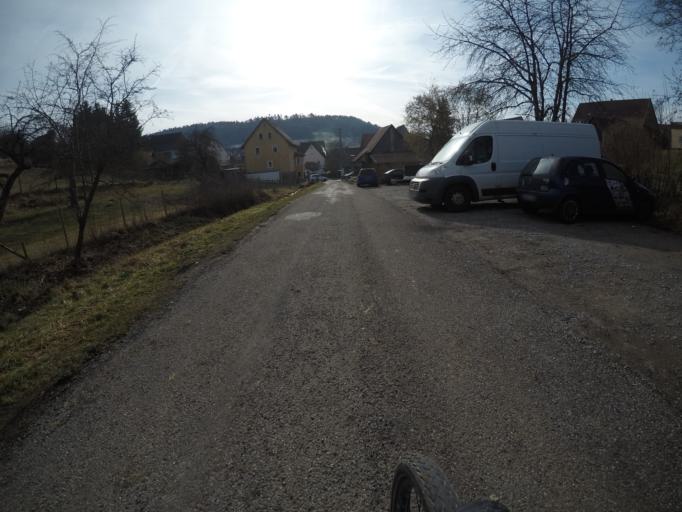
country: DE
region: Baden-Wuerttemberg
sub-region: Karlsruhe Region
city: Wildberg
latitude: 48.6515
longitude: 8.7743
